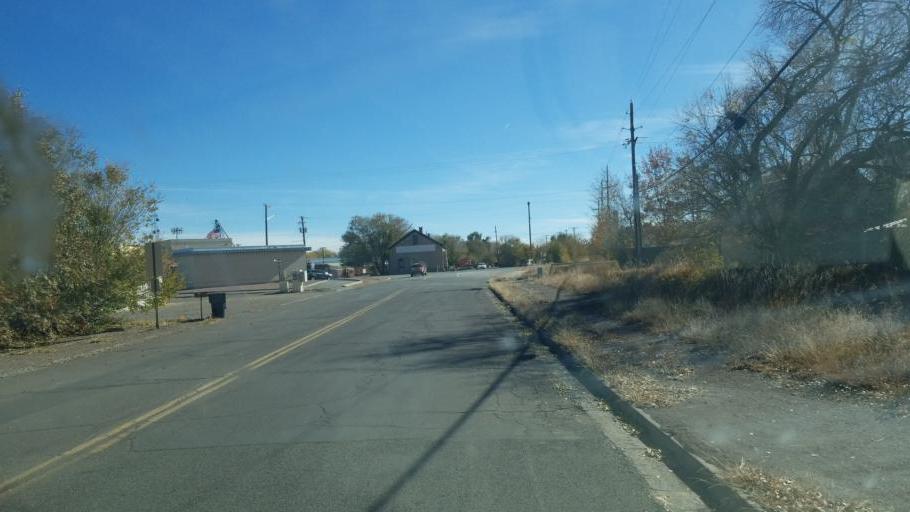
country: US
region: Colorado
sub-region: Rio Grande County
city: Monte Vista
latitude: 37.5817
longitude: -106.1508
